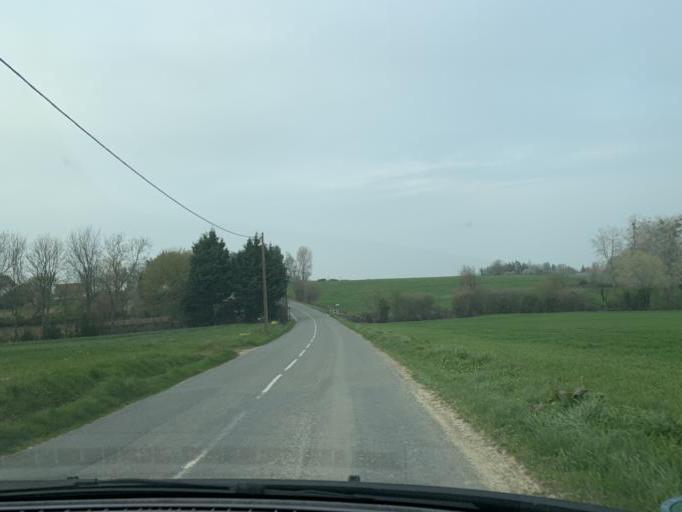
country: FR
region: Nord-Pas-de-Calais
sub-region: Departement du Pas-de-Calais
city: Longfosse
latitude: 50.6947
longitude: 1.7748
